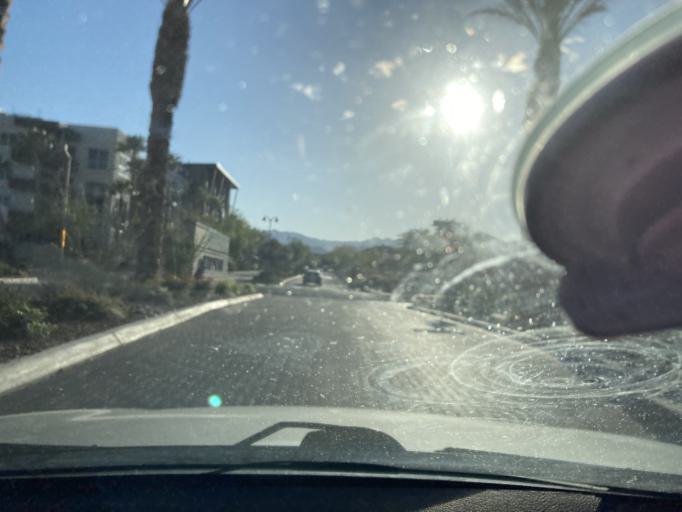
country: US
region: Nevada
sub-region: Clark County
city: Summerlin South
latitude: 36.1573
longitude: -115.3435
